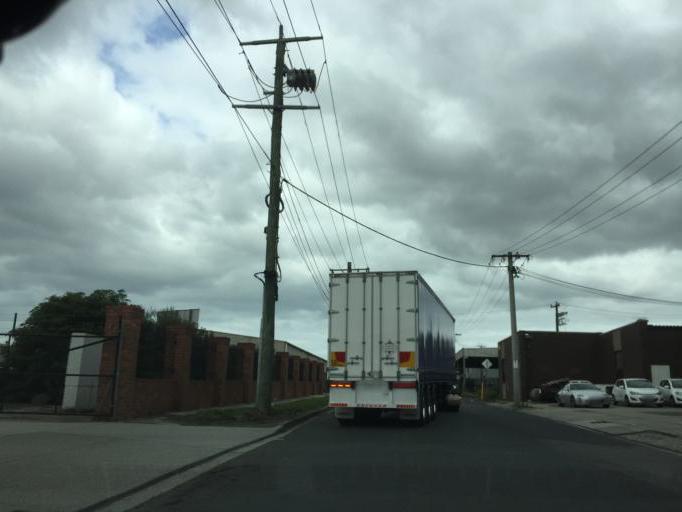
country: AU
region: Victoria
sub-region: Brimbank
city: Brooklyn
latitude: -37.8064
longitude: 144.8520
